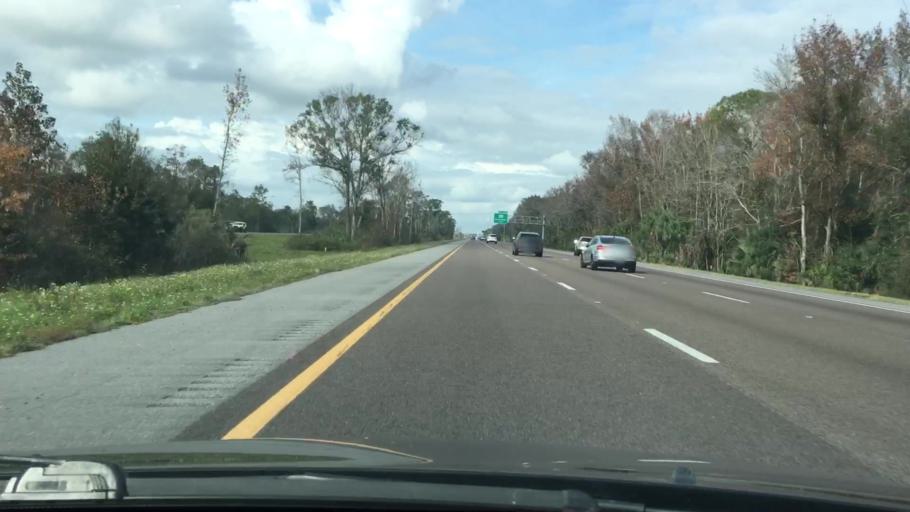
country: US
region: Florida
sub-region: Volusia County
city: Edgewater
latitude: 28.9298
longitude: -80.9407
